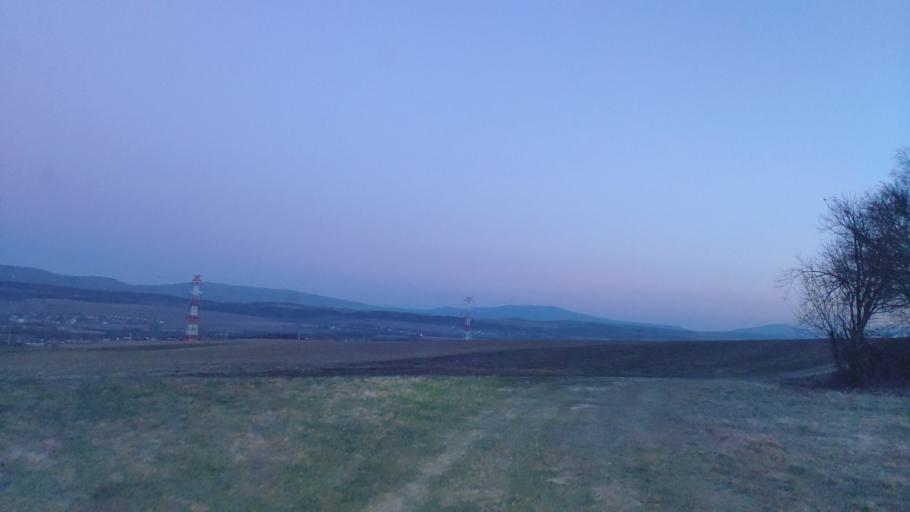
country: SK
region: Kosicky
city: Kosice
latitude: 48.8323
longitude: 21.2595
